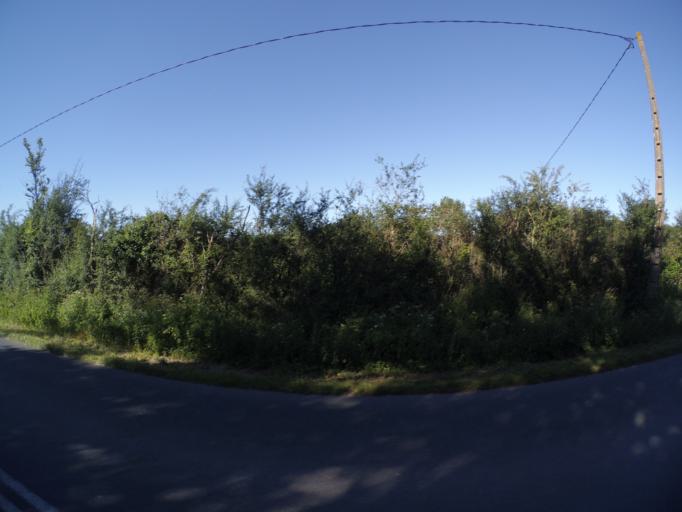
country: FR
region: Pays de la Loire
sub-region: Departement de la Vendee
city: La Boissiere-de-Montaigu
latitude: 46.9139
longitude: -1.1494
